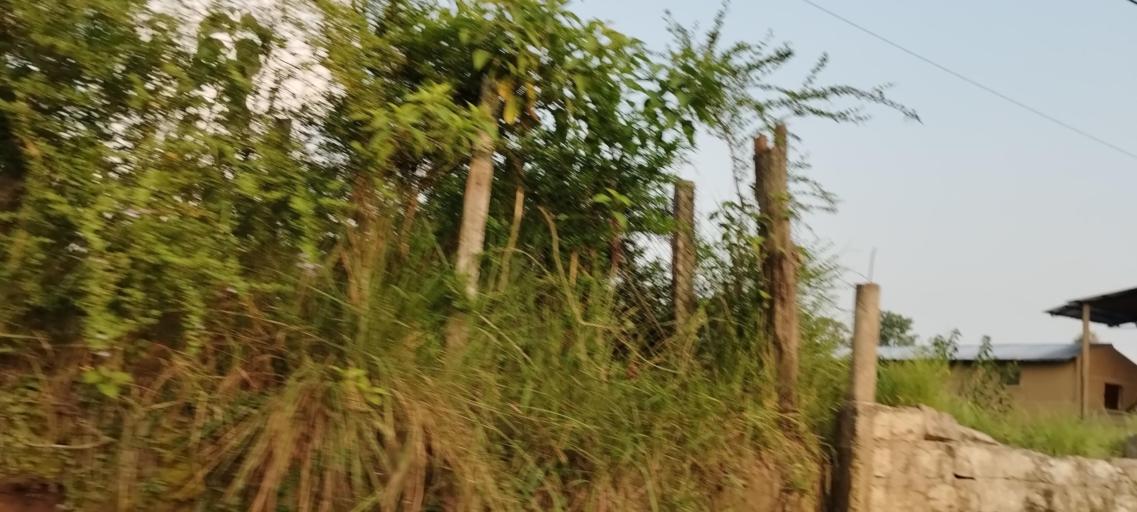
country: NP
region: Far Western
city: Tikapur
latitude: 28.4497
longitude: 81.2393
